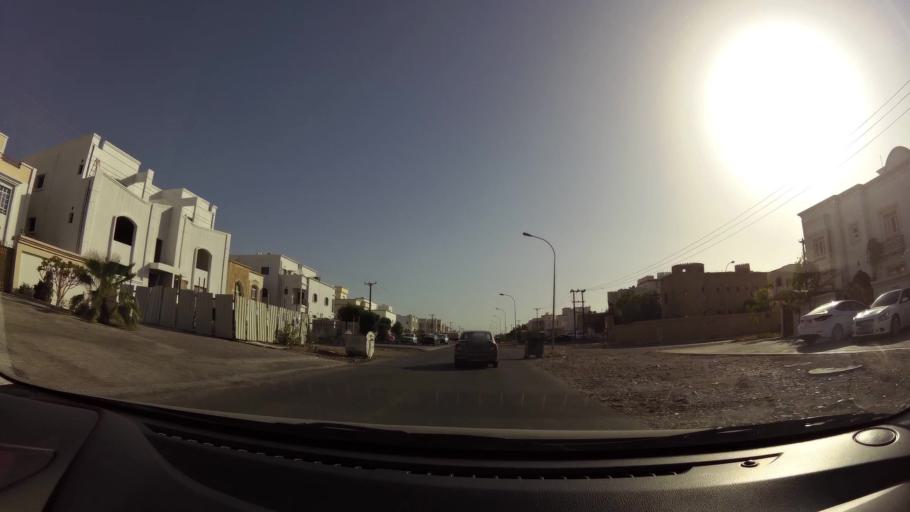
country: OM
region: Muhafazat Masqat
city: As Sib al Jadidah
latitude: 23.5998
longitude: 58.2108
